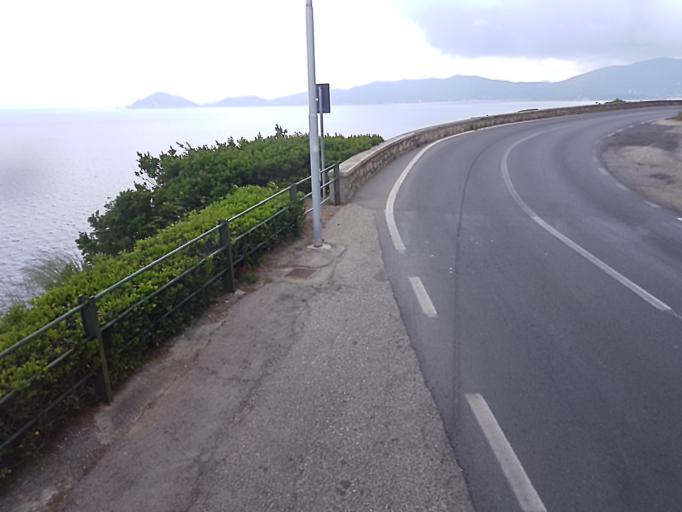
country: IT
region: Tuscany
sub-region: Provincia di Livorno
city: Marciana Marina
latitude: 42.8067
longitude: 10.2053
